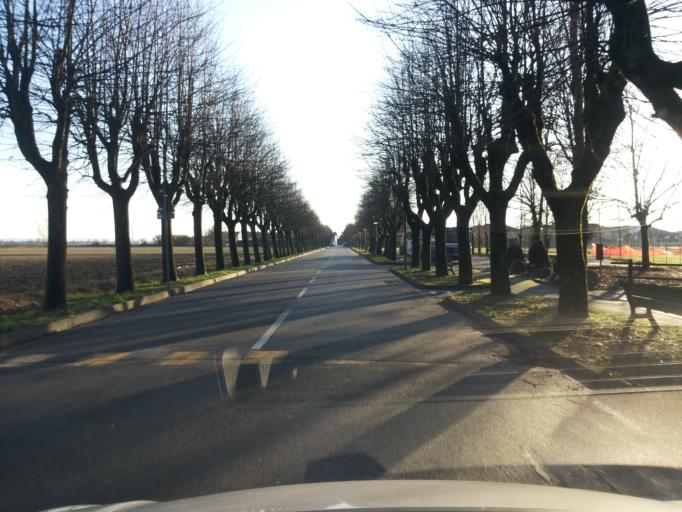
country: IT
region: Piedmont
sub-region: Provincia di Vercelli
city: Lignana
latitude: 45.2898
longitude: 8.3479
